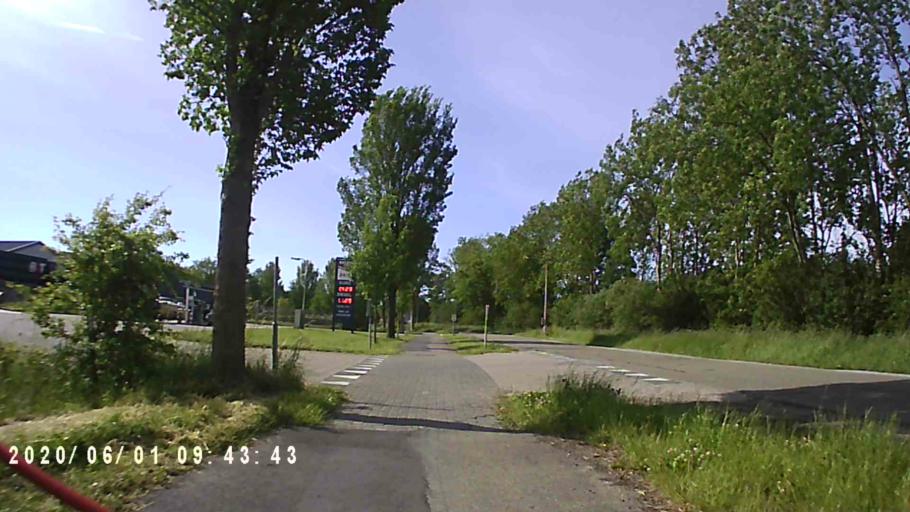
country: NL
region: Friesland
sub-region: Menameradiel
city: Menaam
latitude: 53.2398
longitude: 5.6839
